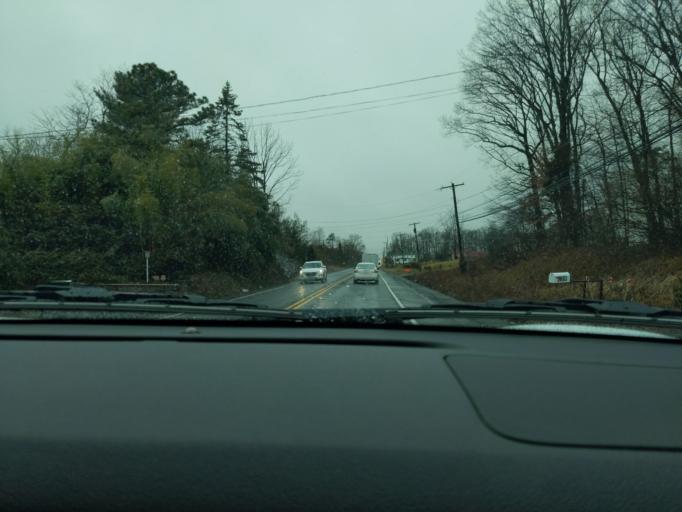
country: US
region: Pennsylvania
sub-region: Bucks County
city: Dublin
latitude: 40.3575
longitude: -75.1781
